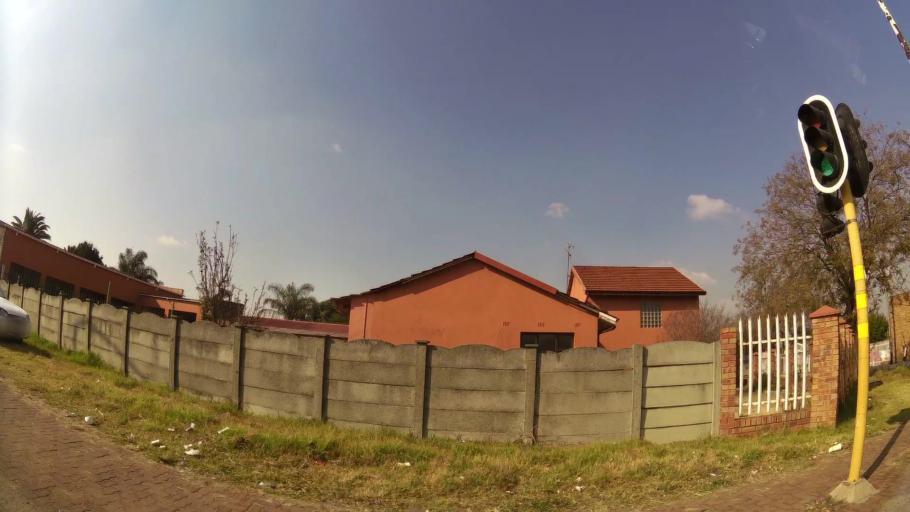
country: ZA
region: Gauteng
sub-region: Ekurhuleni Metropolitan Municipality
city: Boksburg
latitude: -26.1894
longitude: 28.2538
